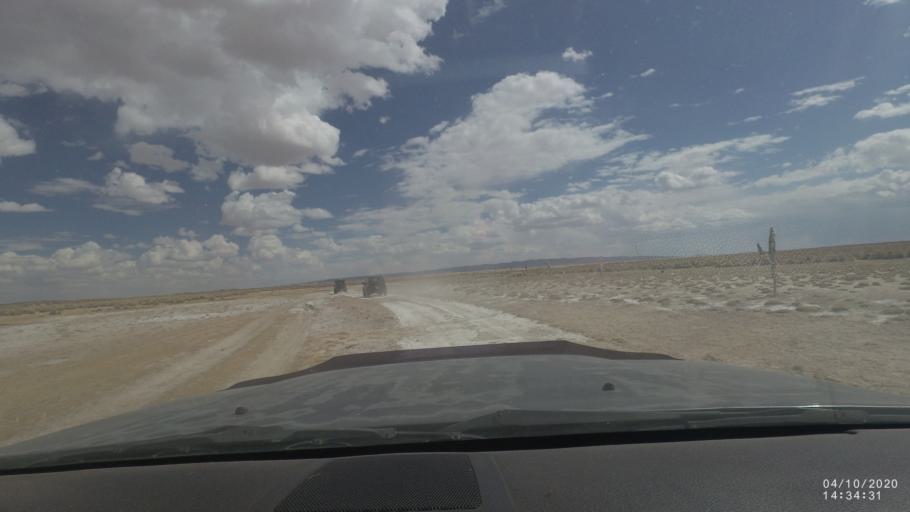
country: BO
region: Oruro
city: Poopo
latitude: -18.6713
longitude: -67.4694
